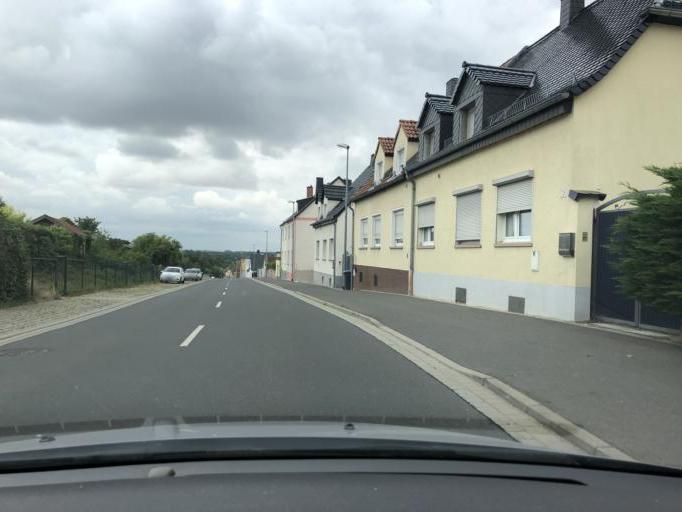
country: DE
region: Saxony-Anhalt
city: Ermlitz
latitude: 51.3960
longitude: 12.1887
